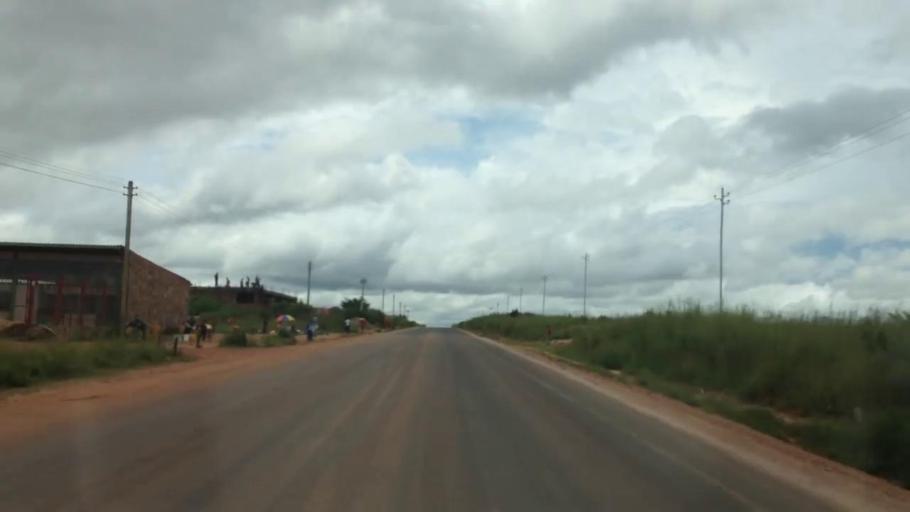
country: CD
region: Katanga
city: Kolwezi
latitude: -10.7435
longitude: 25.5131
